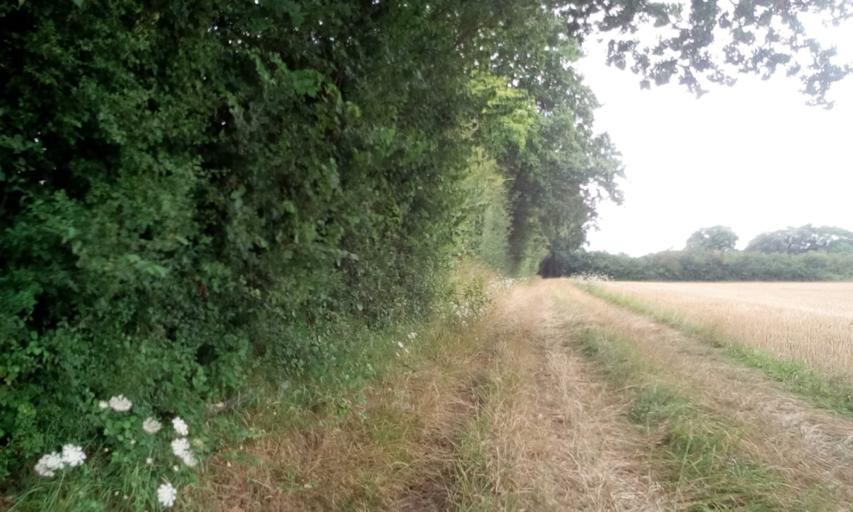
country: FR
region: Lower Normandy
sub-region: Departement du Calvados
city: Troarn
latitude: 49.1656
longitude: -0.1897
